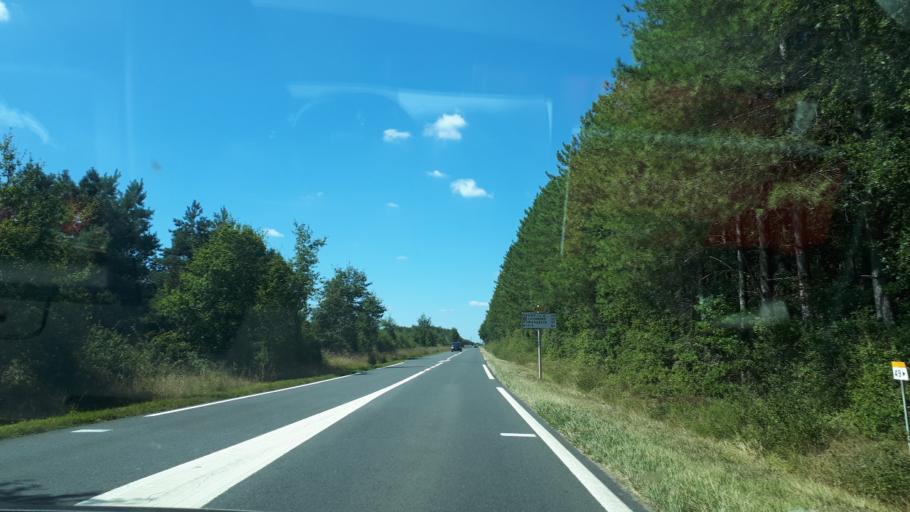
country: FR
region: Centre
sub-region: Departement du Loir-et-Cher
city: Lamotte-Beuvron
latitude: 47.5812
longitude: 1.9831
